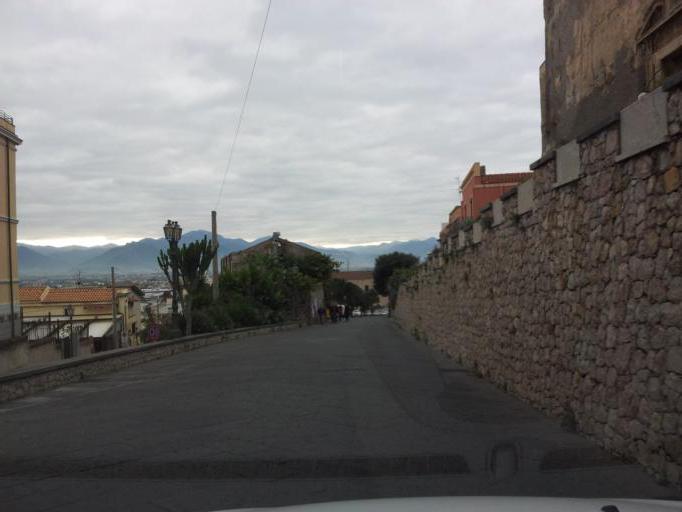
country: IT
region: Sicily
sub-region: Messina
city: Milazzo
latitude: 38.2287
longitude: 15.2425
